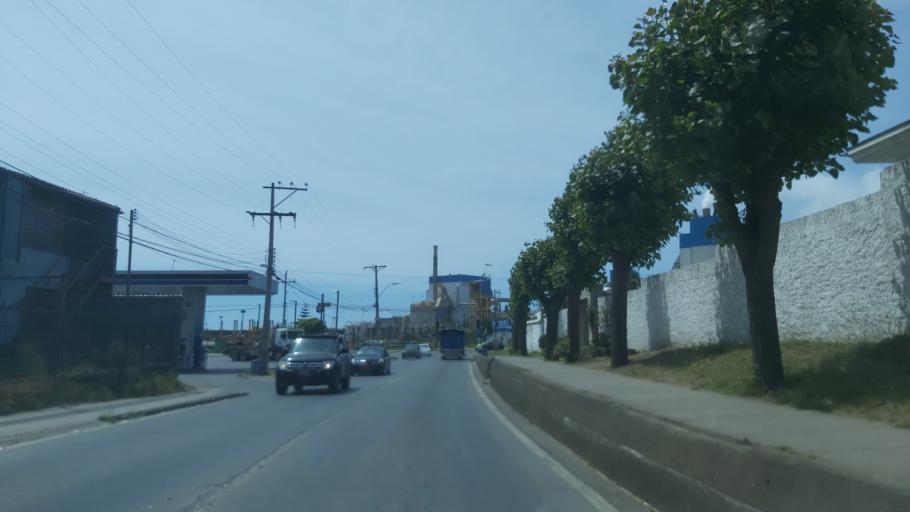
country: CL
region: Maule
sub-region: Provincia de Talca
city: Constitucion
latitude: -35.3279
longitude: -72.4200
